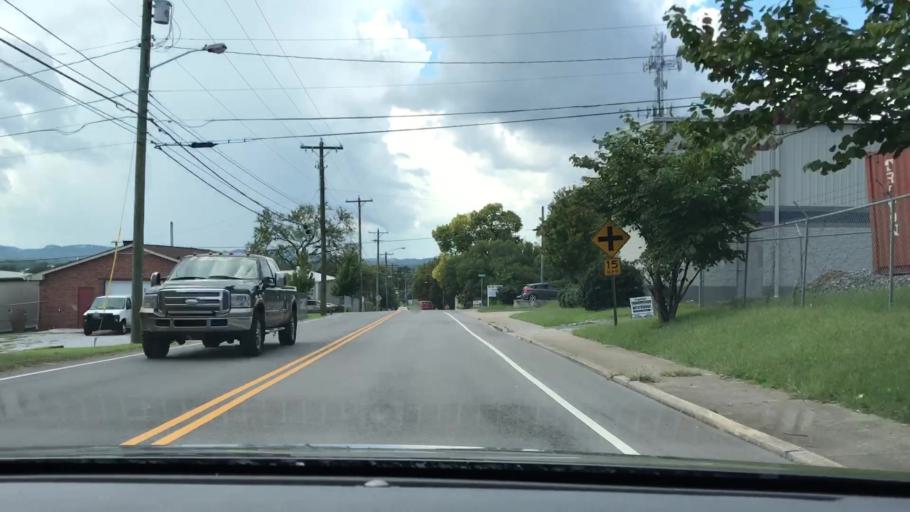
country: US
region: Tennessee
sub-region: Davidson County
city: Oak Hill
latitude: 36.1199
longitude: -86.7528
